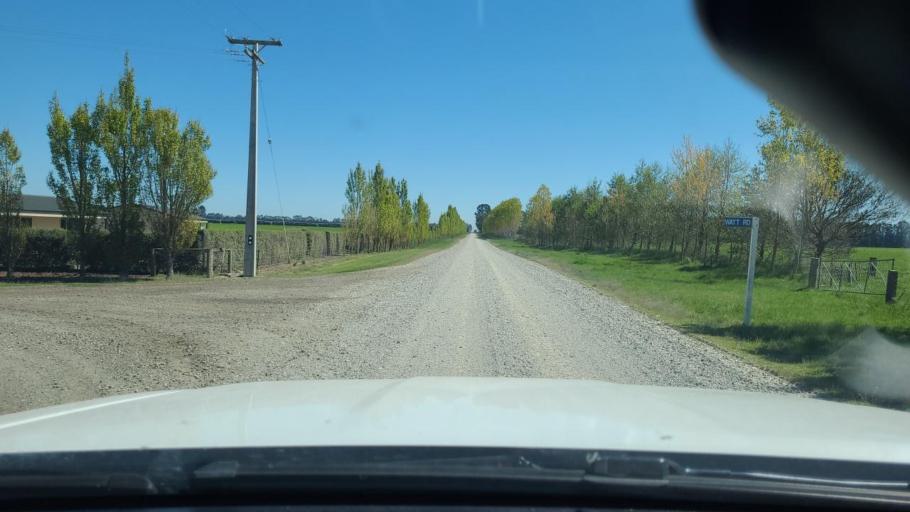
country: NZ
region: Southland
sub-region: Gore District
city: Gore
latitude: -45.7919
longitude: 168.7218
